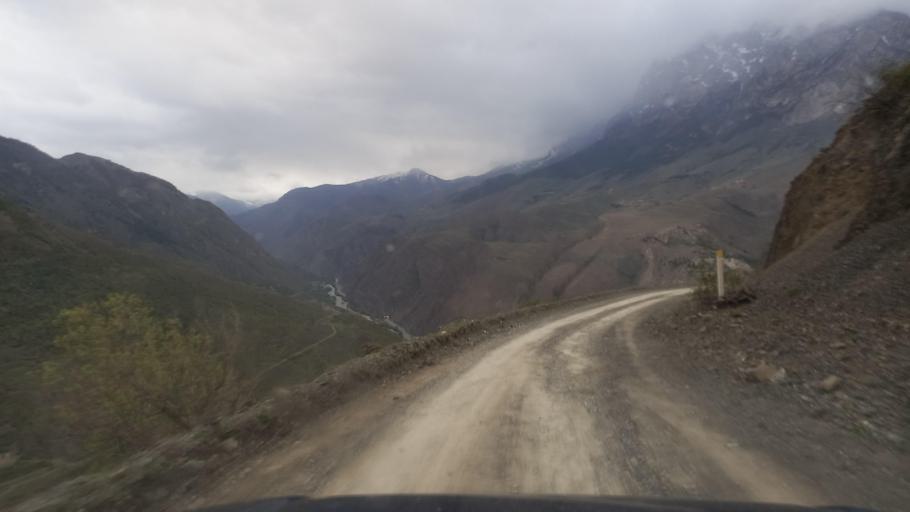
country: RU
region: North Ossetia
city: Mizur
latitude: 42.8556
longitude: 44.1607
